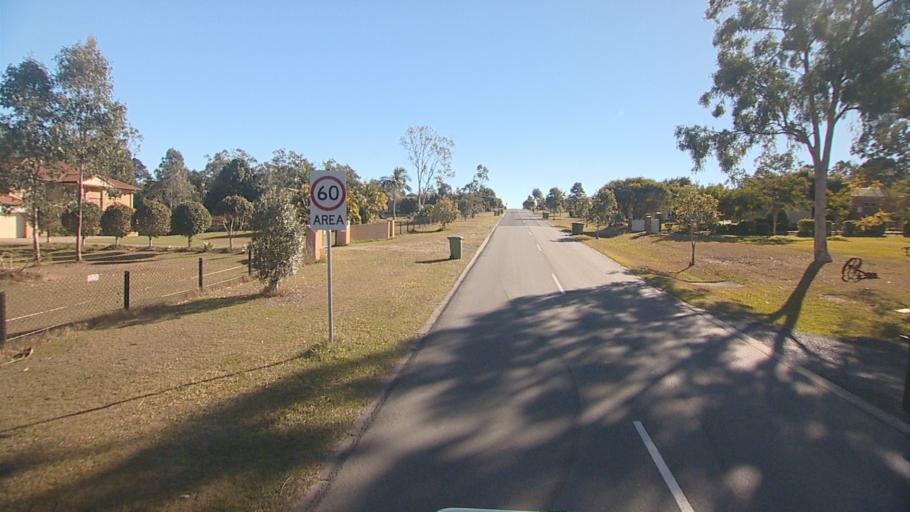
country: AU
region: Queensland
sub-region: Logan
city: North Maclean
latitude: -27.7476
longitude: 152.9677
